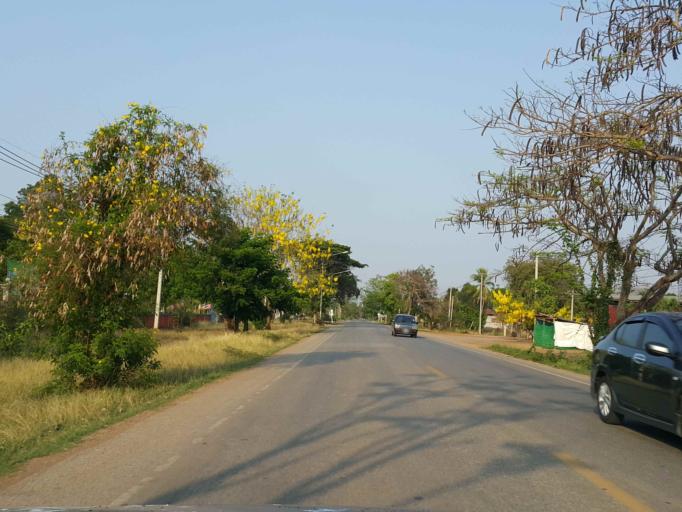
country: TH
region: Sukhothai
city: Sawankhalok
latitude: 17.3072
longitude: 99.7825
